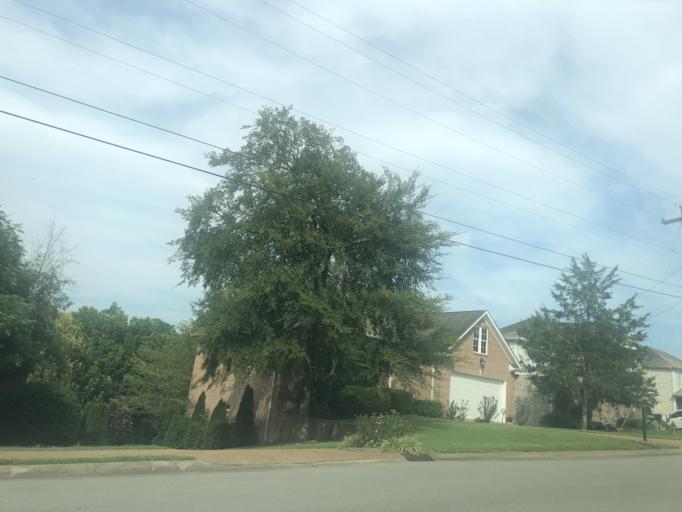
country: US
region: Tennessee
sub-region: Wilson County
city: Green Hill
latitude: 36.1801
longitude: -86.5848
